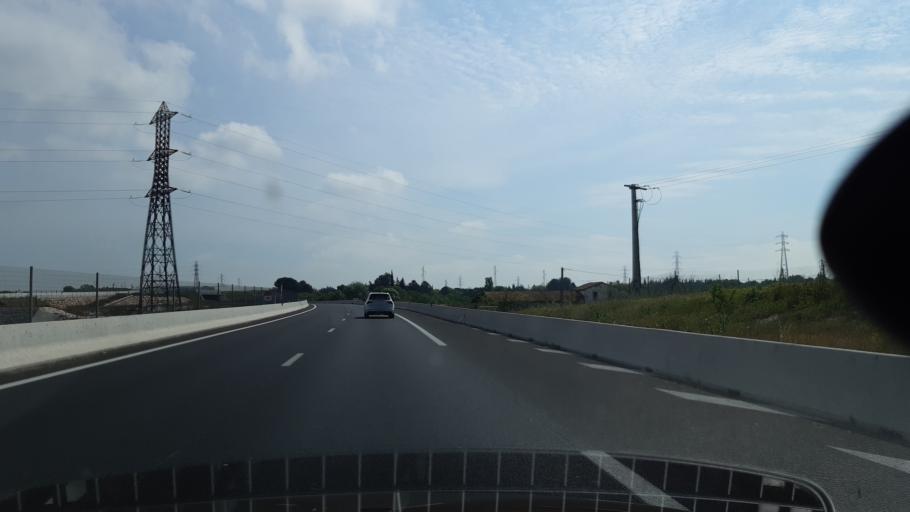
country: FR
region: Languedoc-Roussillon
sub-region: Departement de l'Herault
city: Saint-Jean-de-Vedas
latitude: 43.5696
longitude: 3.8570
